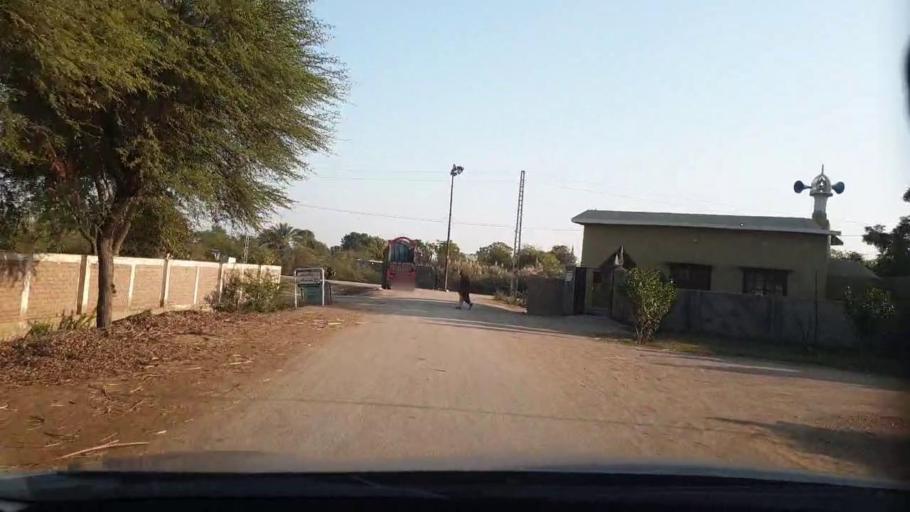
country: PK
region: Sindh
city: Berani
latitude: 25.6361
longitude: 68.8074
